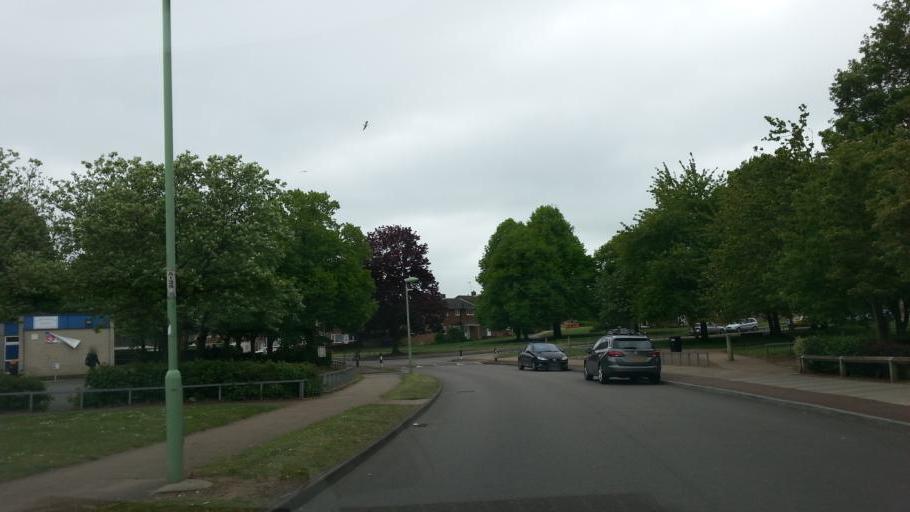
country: GB
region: England
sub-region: Suffolk
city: Bury St Edmunds
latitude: 52.2583
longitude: 0.6959
